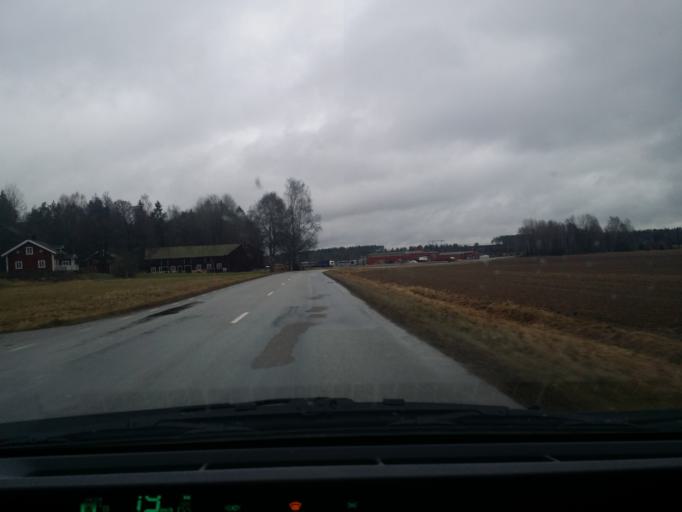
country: SE
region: Vaestmanland
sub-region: Vasteras
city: Skultuna
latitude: 59.8045
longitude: 16.5244
